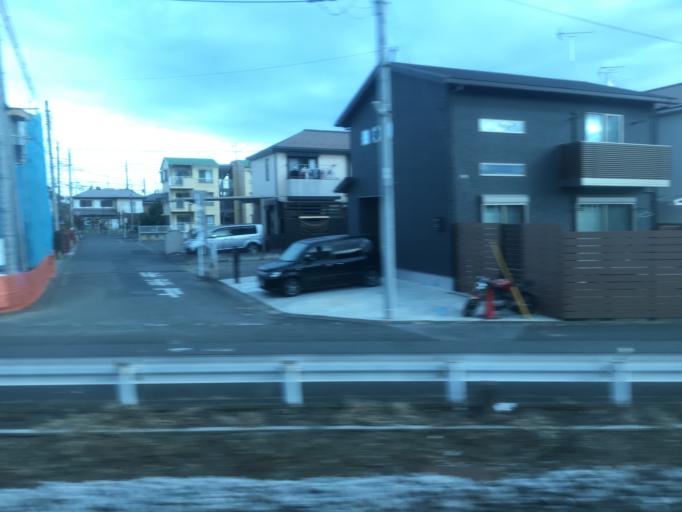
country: JP
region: Saitama
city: Fukiage-fujimi
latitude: 36.0811
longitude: 139.4814
